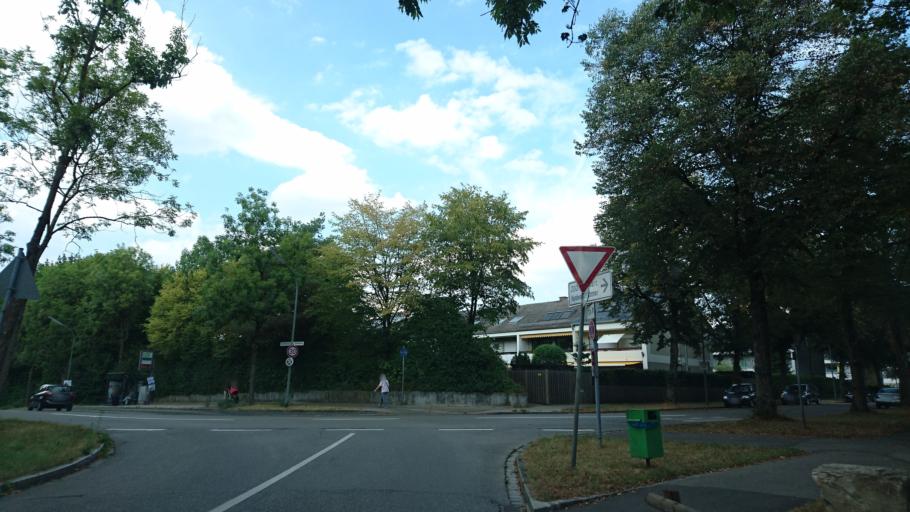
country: DE
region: Bavaria
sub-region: Swabia
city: Augsburg
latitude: 48.3521
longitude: 10.9173
